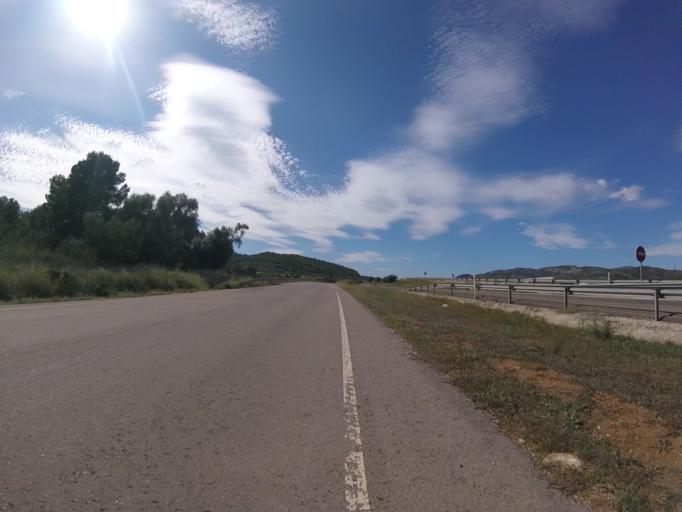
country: ES
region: Valencia
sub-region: Provincia de Castello
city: Peniscola
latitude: 40.3955
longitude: 0.3607
